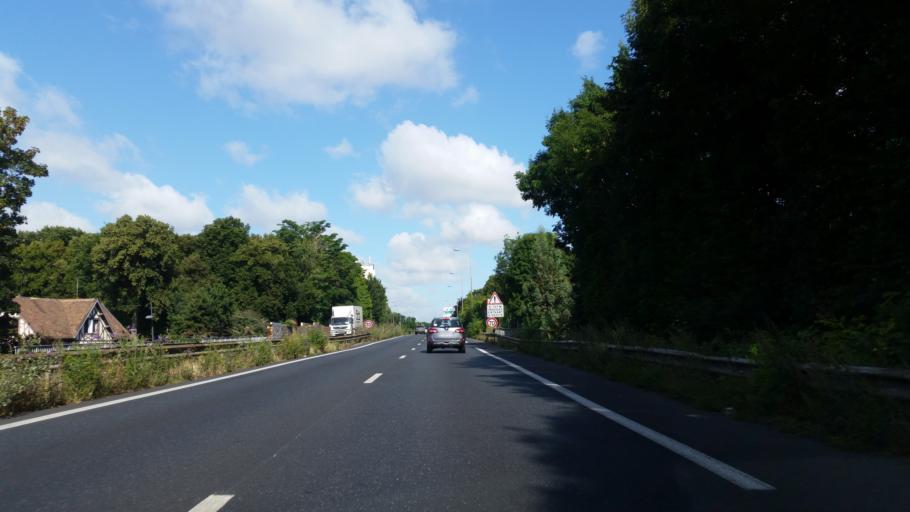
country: FR
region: Lower Normandy
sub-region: Departement du Calvados
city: Mondeville
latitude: 49.1778
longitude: -0.3184
